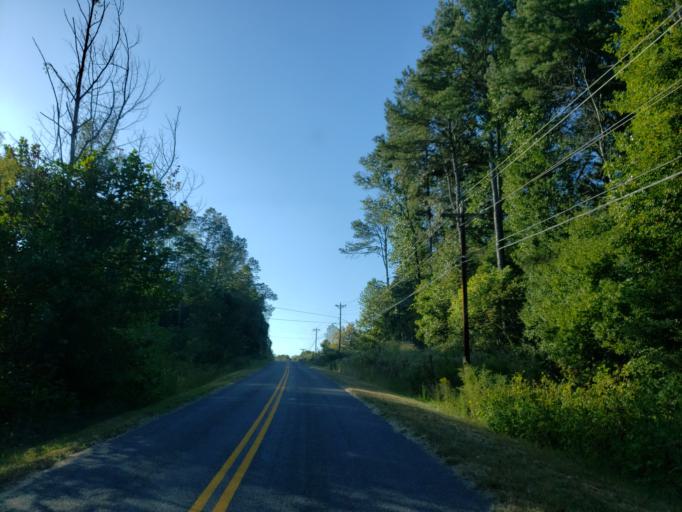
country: US
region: Georgia
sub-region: Pickens County
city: Nelson
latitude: 34.3852
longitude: -84.4037
